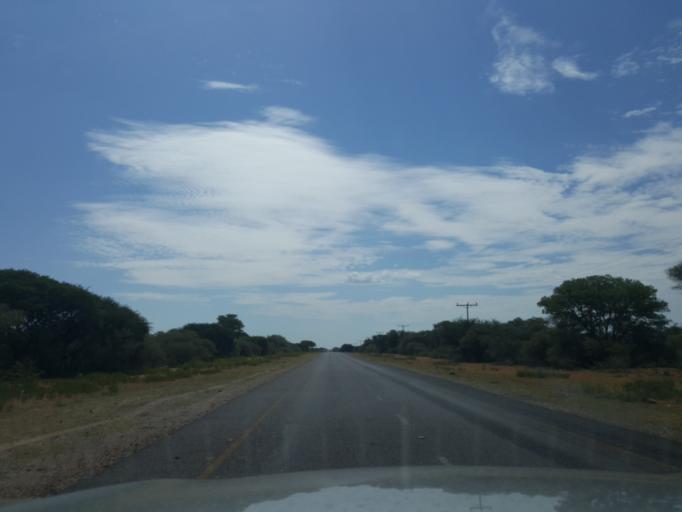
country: BW
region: Kweneng
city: Letlhakeng
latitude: -24.1623
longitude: 25.1693
